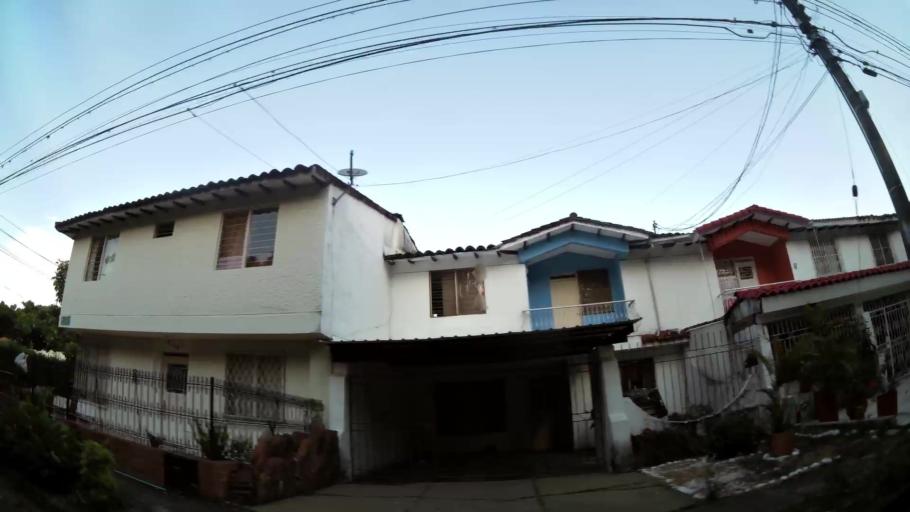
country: CO
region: Valle del Cauca
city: Cali
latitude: 3.4058
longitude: -76.5541
